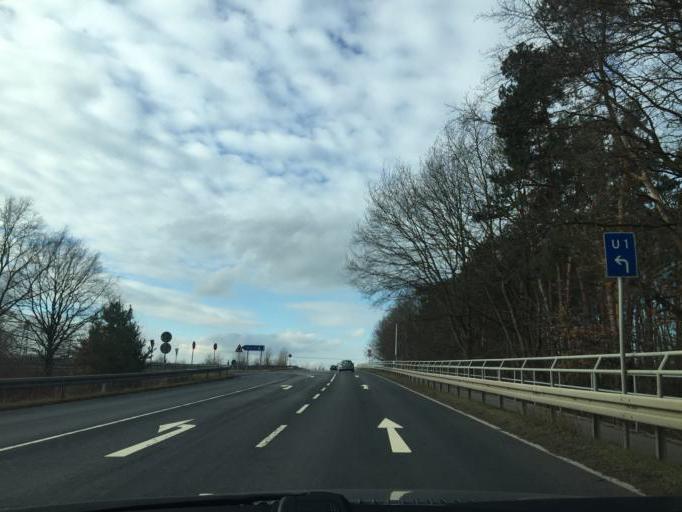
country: DE
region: Saxony
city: Radeburg
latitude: 51.2125
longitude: 13.7396
